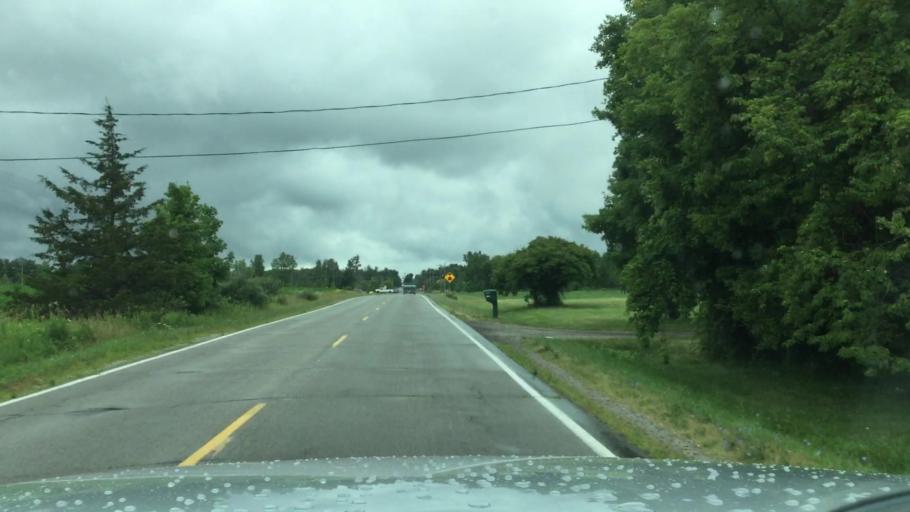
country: US
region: Michigan
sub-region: Genesee County
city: Clio
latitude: 43.1217
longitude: -83.7738
